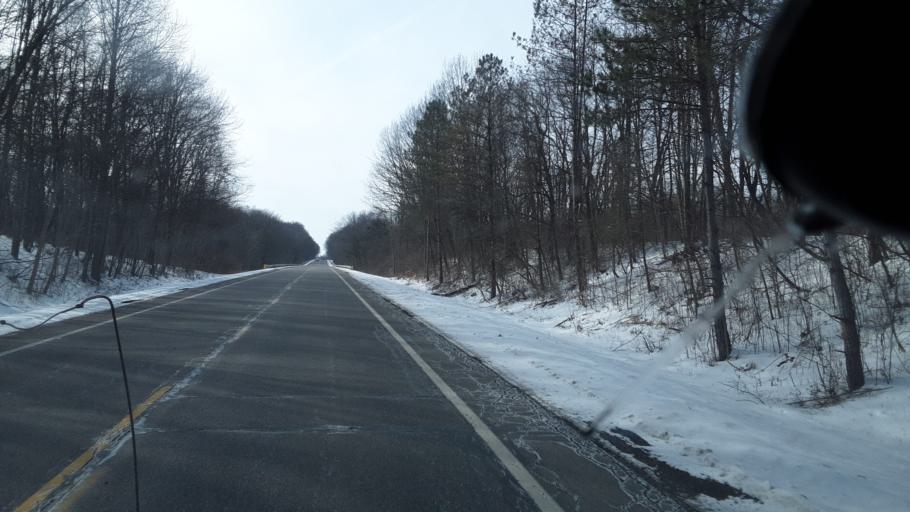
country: US
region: Ohio
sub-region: Stark County
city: Hartville
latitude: 41.0333
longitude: -81.2834
